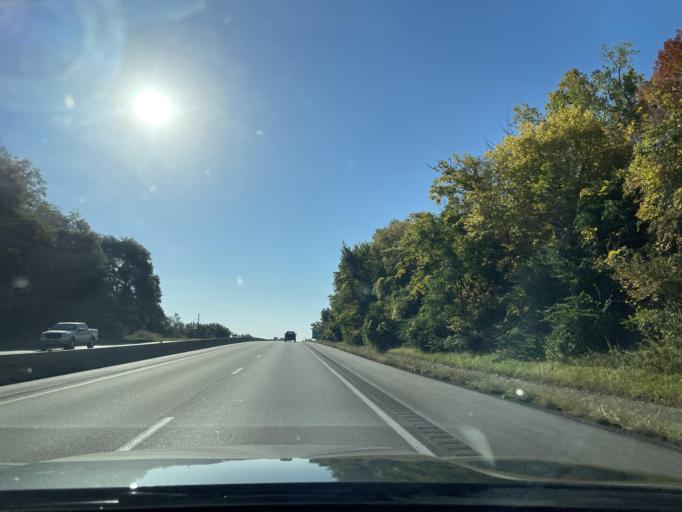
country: US
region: Missouri
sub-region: Buchanan County
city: Saint Joseph
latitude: 39.7768
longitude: -94.8647
